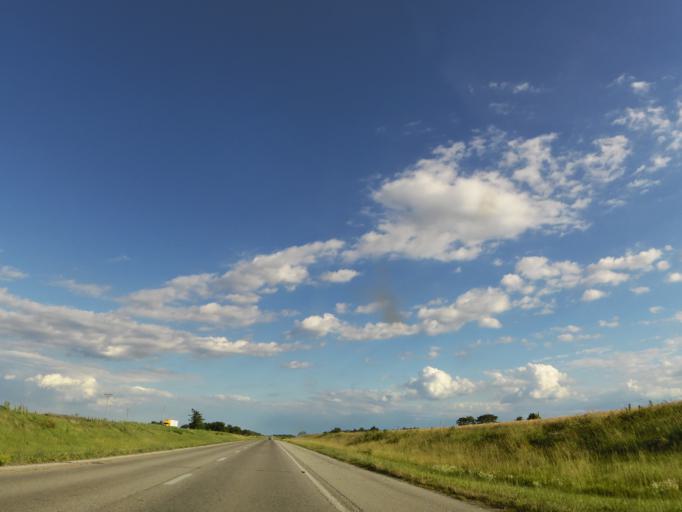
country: US
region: Missouri
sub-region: Lincoln County
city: Elsberry
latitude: 39.2028
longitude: -91.0001
